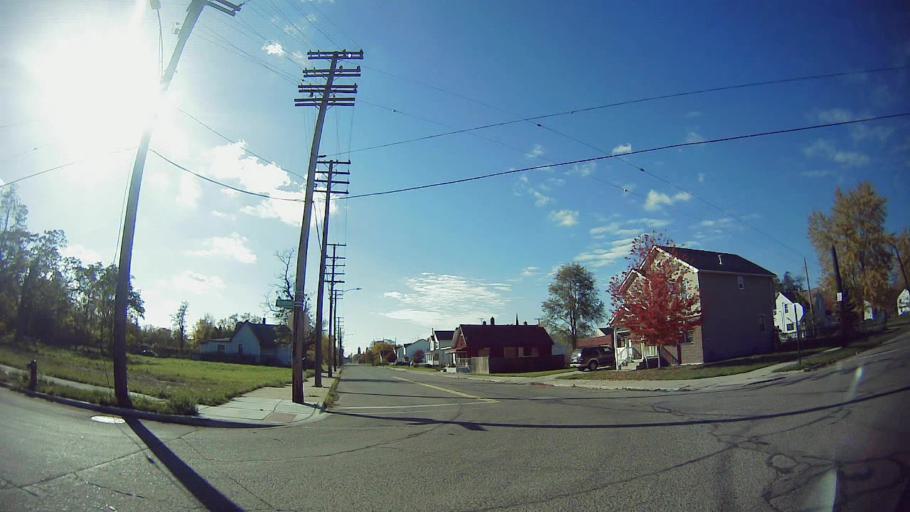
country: US
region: Michigan
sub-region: Wayne County
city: Detroit
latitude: 42.3383
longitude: -83.1063
